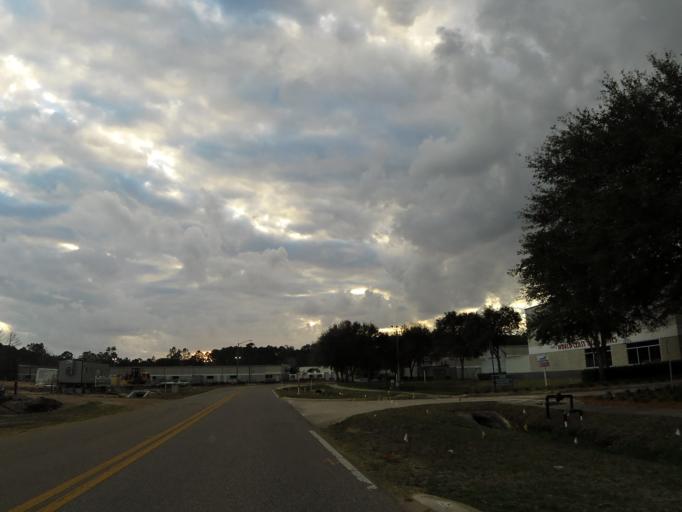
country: US
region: Florida
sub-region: Saint Johns County
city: Fruit Cove
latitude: 30.1859
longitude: -81.5720
